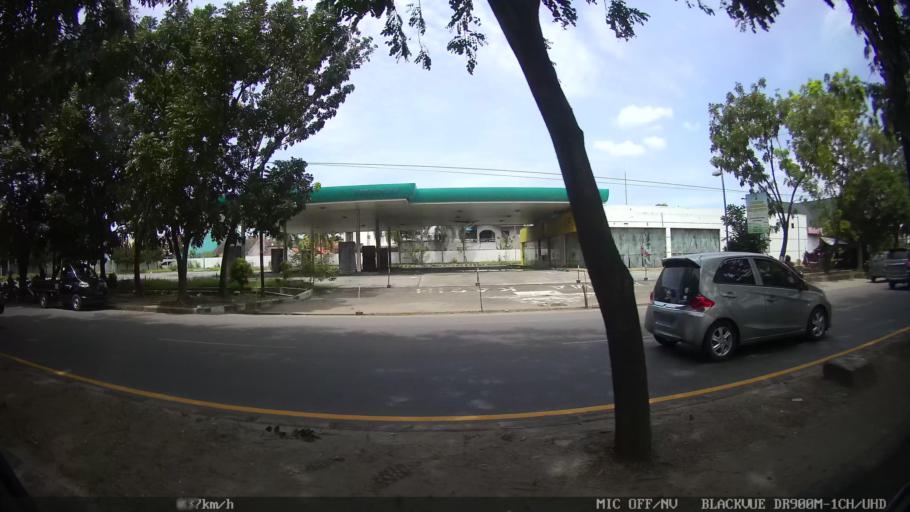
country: ID
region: North Sumatra
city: Sunggal
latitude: 3.5694
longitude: 98.6261
